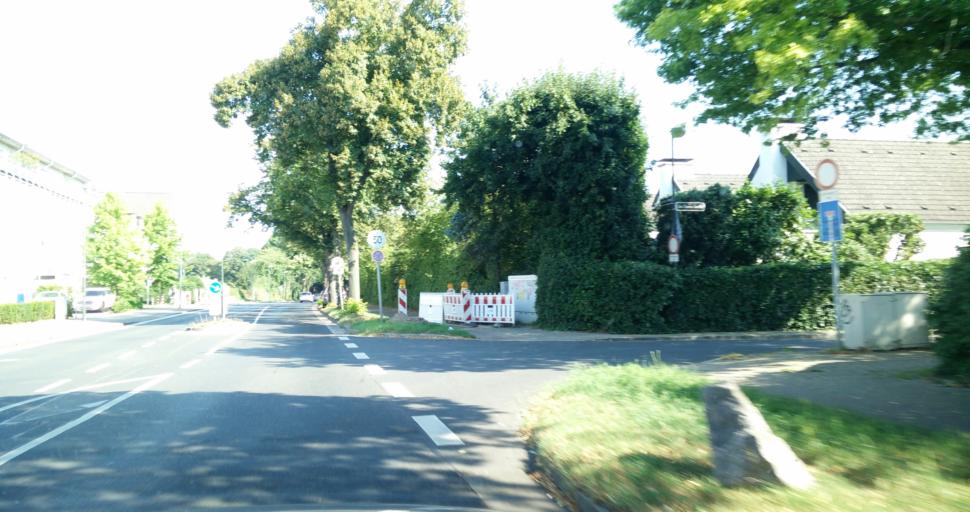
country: DE
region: North Rhine-Westphalia
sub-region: Regierungsbezirk Dusseldorf
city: Meerbusch
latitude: 51.3110
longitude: 6.7435
